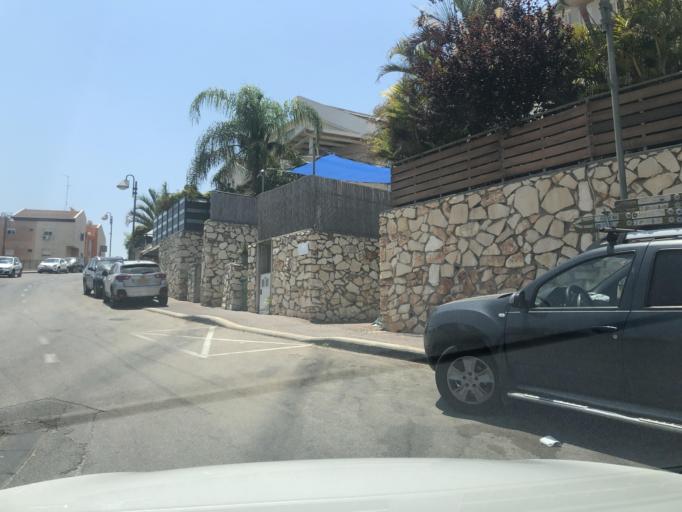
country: IL
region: Haifa
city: Daliyat el Karmil
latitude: 32.6361
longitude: 35.0934
